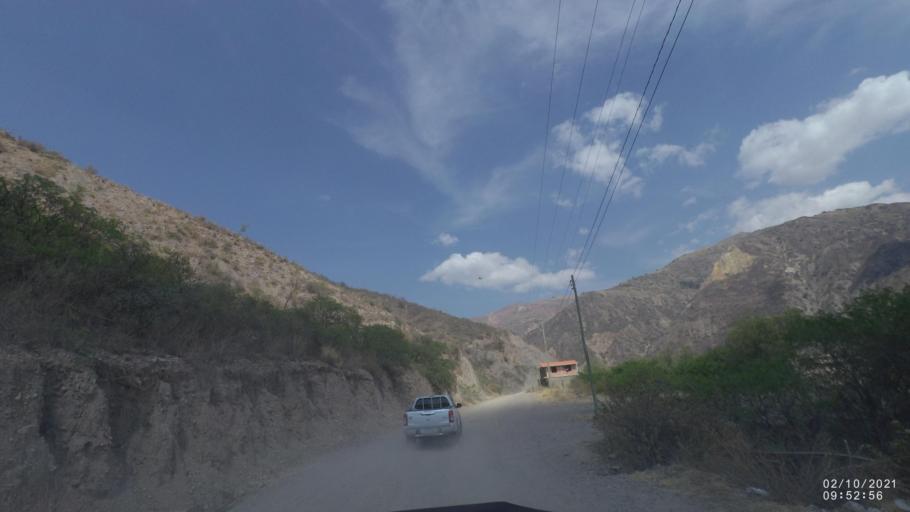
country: BO
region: Cochabamba
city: Irpa Irpa
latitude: -17.8010
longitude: -66.3464
